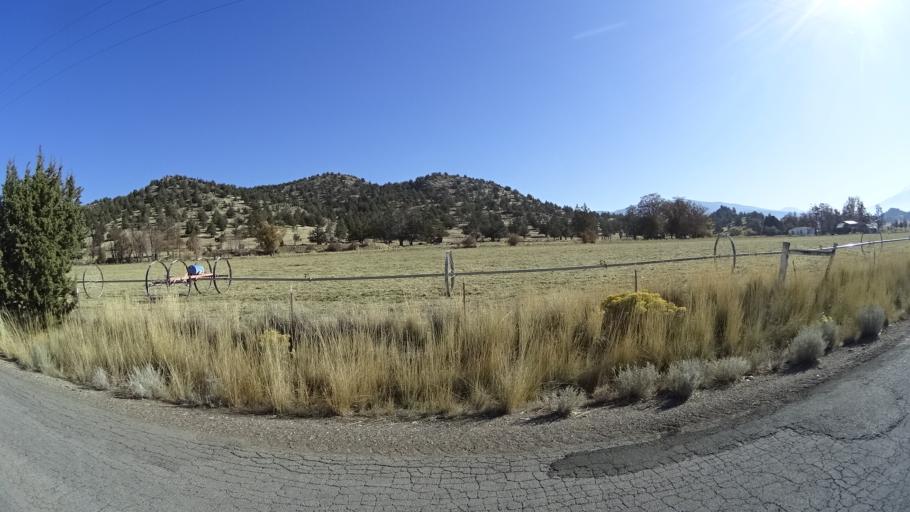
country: US
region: California
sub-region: Siskiyou County
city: Montague
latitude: 41.7067
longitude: -122.3792
